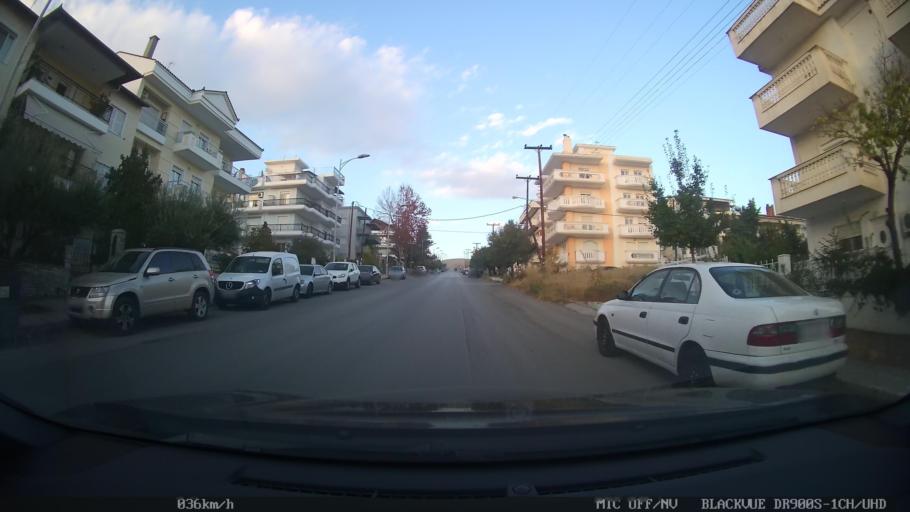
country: GR
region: Central Macedonia
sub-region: Nomos Thessalonikis
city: Pylaia
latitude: 40.6107
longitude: 22.9925
